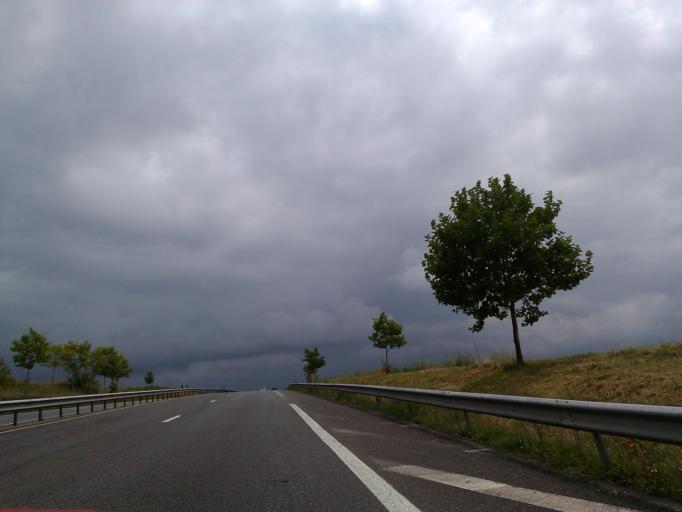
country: FR
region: Poitou-Charentes
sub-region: Departement de la Charente
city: Gensac-la-Pallue
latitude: 45.6703
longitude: -0.2550
